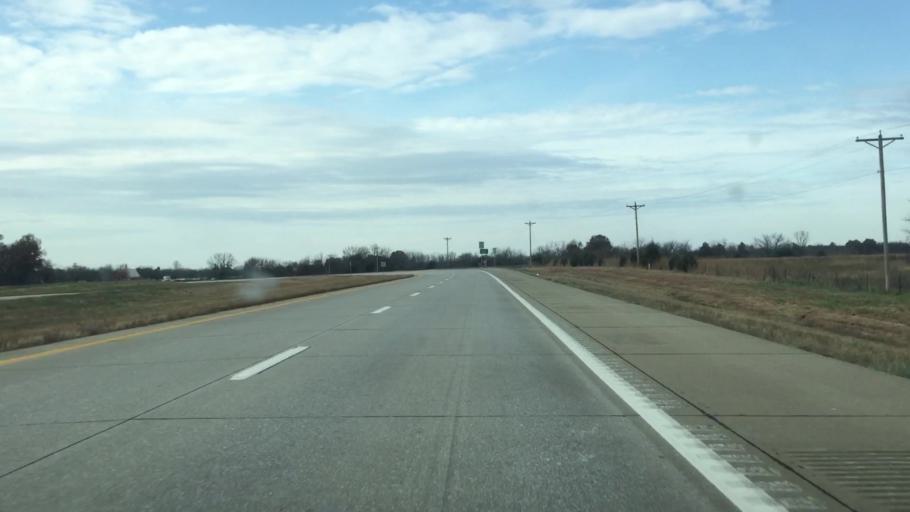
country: US
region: Missouri
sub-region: Henry County
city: Clinton
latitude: 38.4612
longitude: -93.9686
